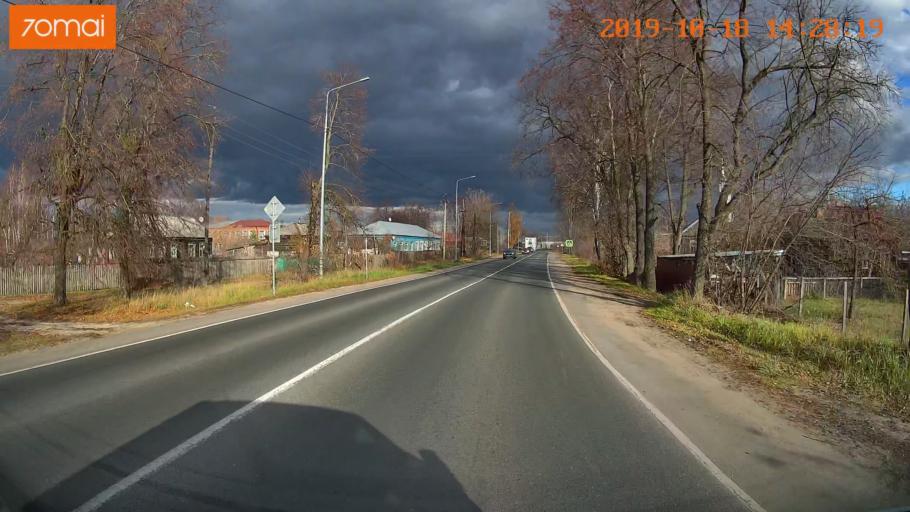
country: RU
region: Rjazan
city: Tuma
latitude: 55.1481
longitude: 40.5506
